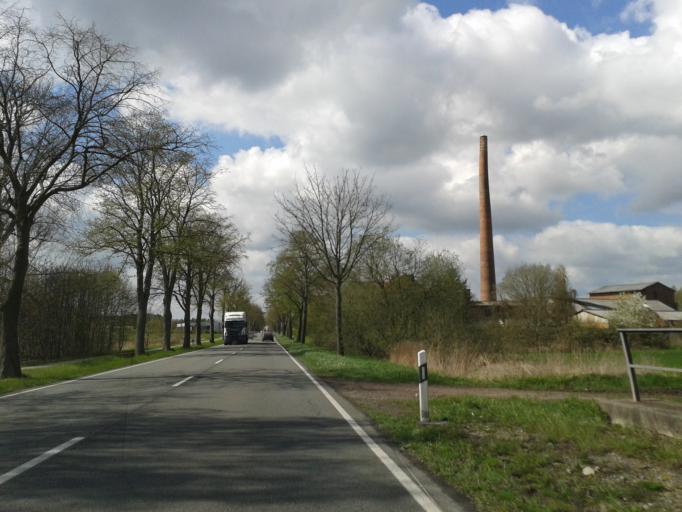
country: DE
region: Saxony-Anhalt
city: Salzwedel
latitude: 52.8634
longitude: 11.1095
